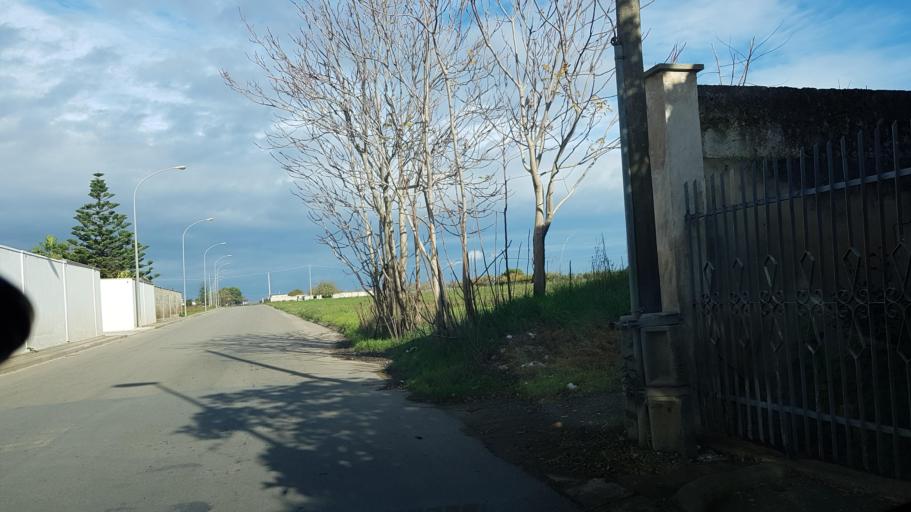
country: IT
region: Apulia
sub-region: Provincia di Brindisi
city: Torre Santa Susanna
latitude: 40.4665
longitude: 17.7448
